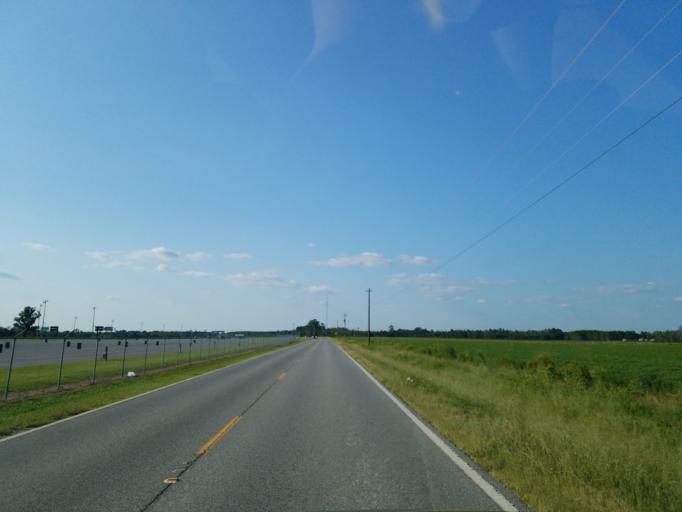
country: US
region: Georgia
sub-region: Lowndes County
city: Hahira
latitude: 31.0645
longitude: -83.3948
